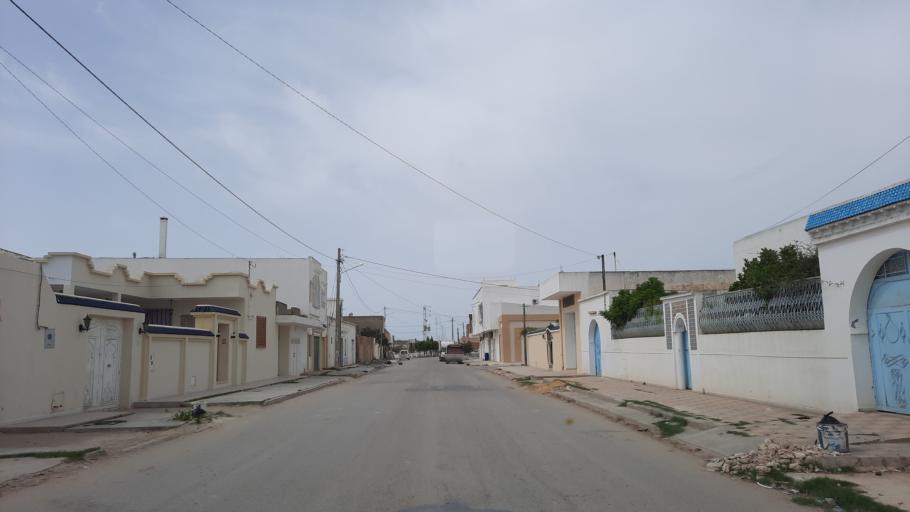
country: TN
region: Al Mahdiyah
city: El Jem
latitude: 35.3008
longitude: 10.7053
